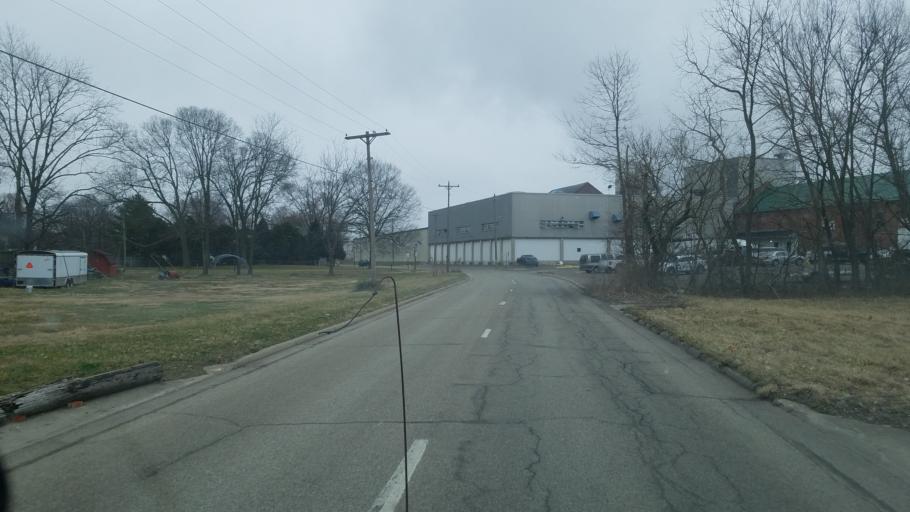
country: US
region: Indiana
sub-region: Wabash County
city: Wabash
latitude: 40.7954
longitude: -85.8317
